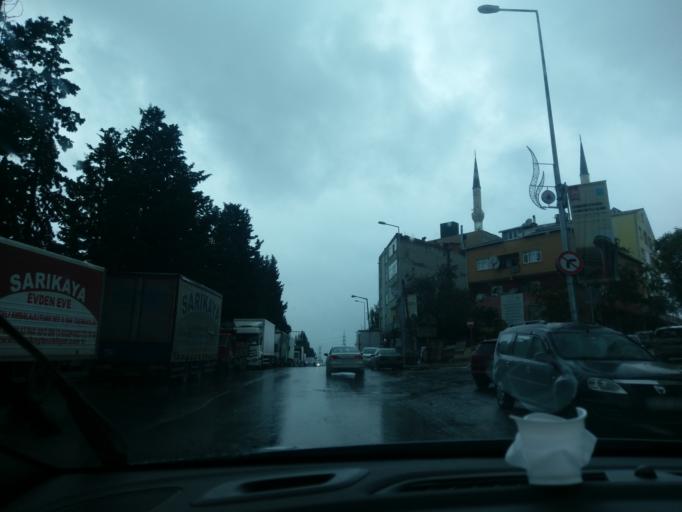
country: TR
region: Istanbul
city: Sisli
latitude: 41.0920
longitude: 28.9673
